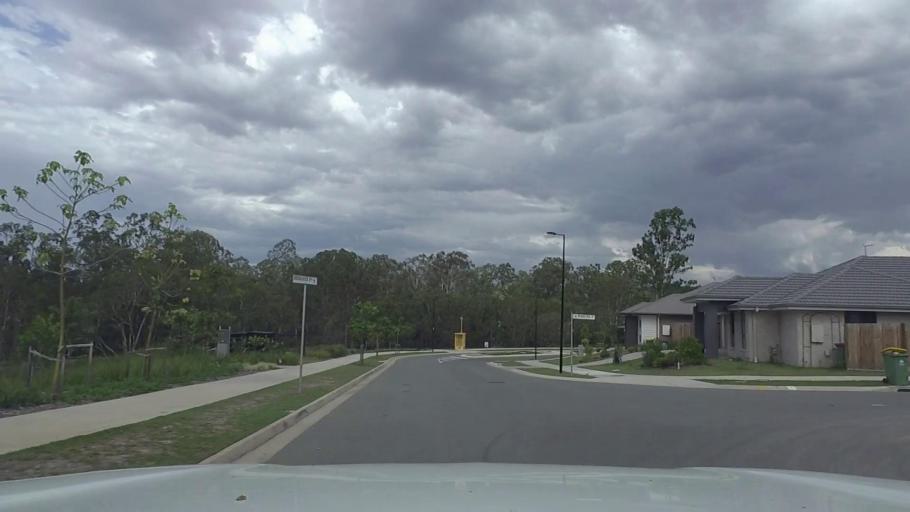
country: AU
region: Queensland
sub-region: Logan
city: Windaroo
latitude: -27.7315
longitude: 153.1664
